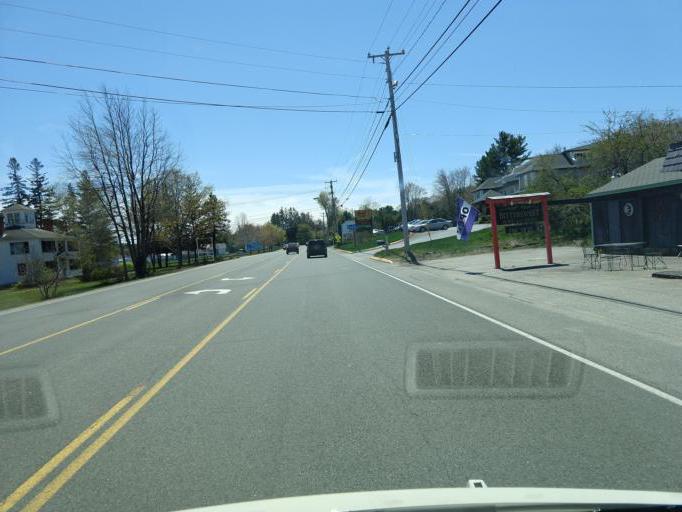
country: US
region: Maine
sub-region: York County
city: Wells Beach Station
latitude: 43.2924
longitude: -70.5899
